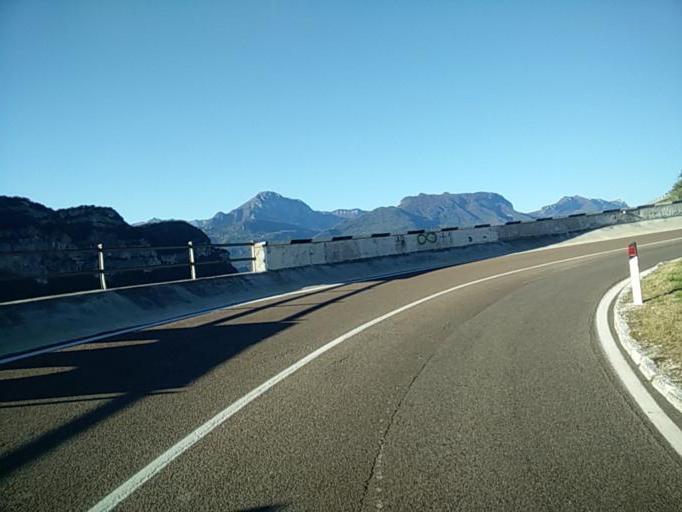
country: IT
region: Trentino-Alto Adige
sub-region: Provincia di Trento
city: Nago-Torbole
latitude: 45.8803
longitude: 10.8850
